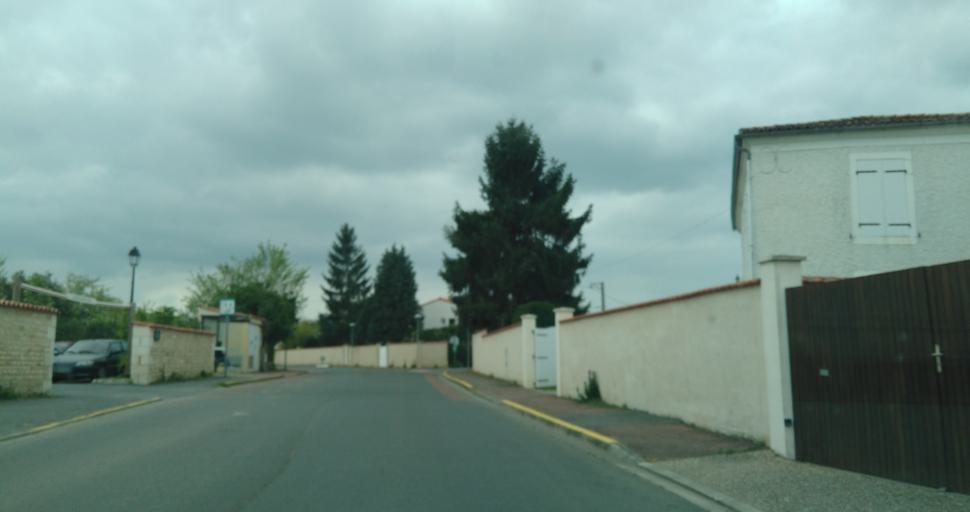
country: FR
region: Poitou-Charentes
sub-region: Departement des Deux-Sevres
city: Coulon
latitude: 46.3236
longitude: -0.5858
